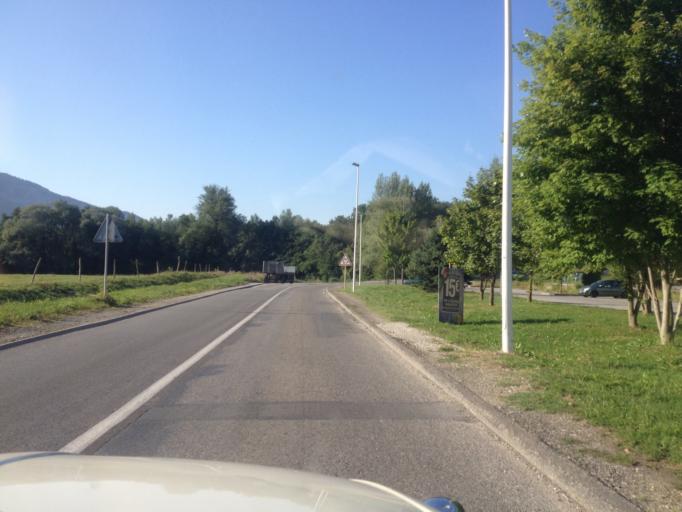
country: FR
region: Rhone-Alpes
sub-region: Departement de la Savoie
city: Drumettaz-Clarafond
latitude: 45.6573
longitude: 5.9142
